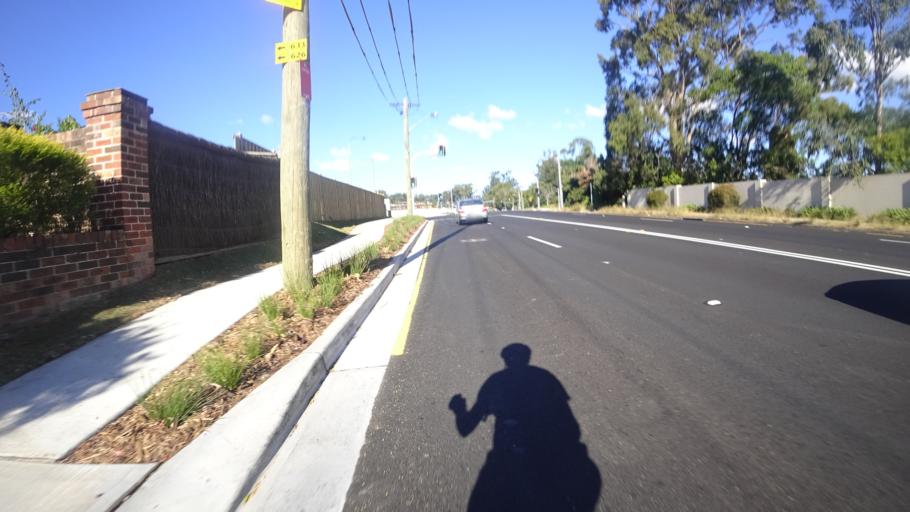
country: AU
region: New South Wales
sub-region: The Hills Shire
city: West Pennant
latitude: -33.7353
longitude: 151.0299
